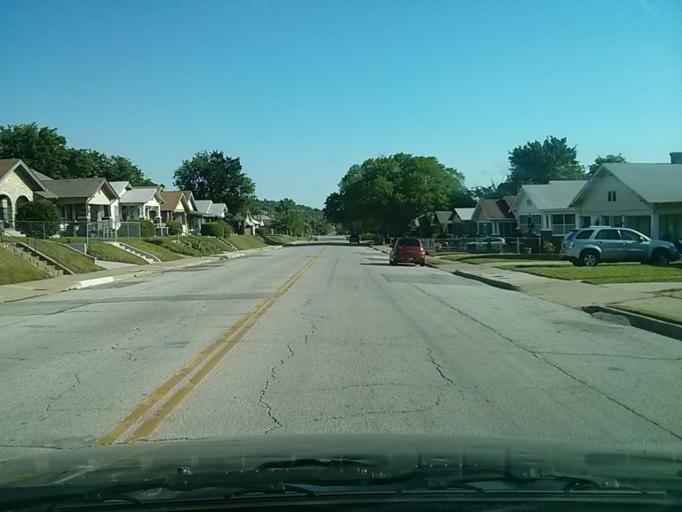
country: US
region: Oklahoma
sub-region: Tulsa County
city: Tulsa
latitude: 36.1738
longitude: -95.9968
